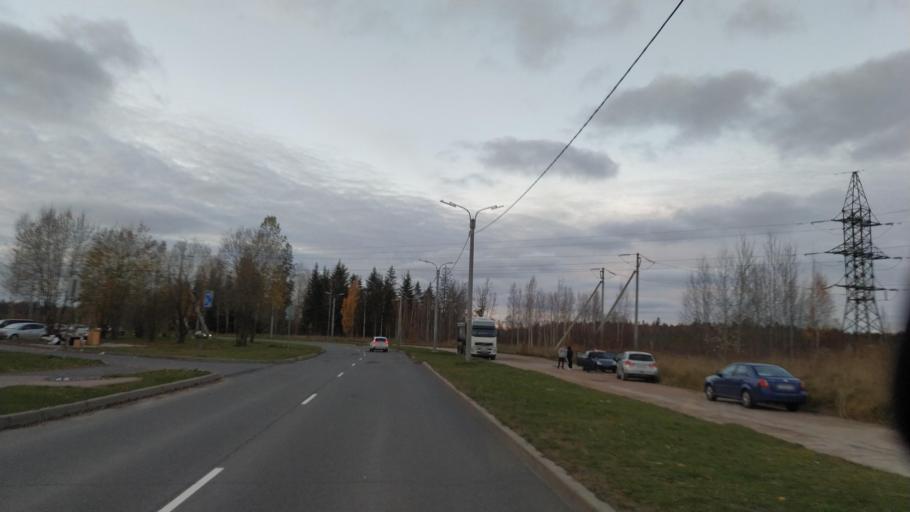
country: RU
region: Leningrad
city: Sosnovyy Bor
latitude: 59.9168
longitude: 29.0923
